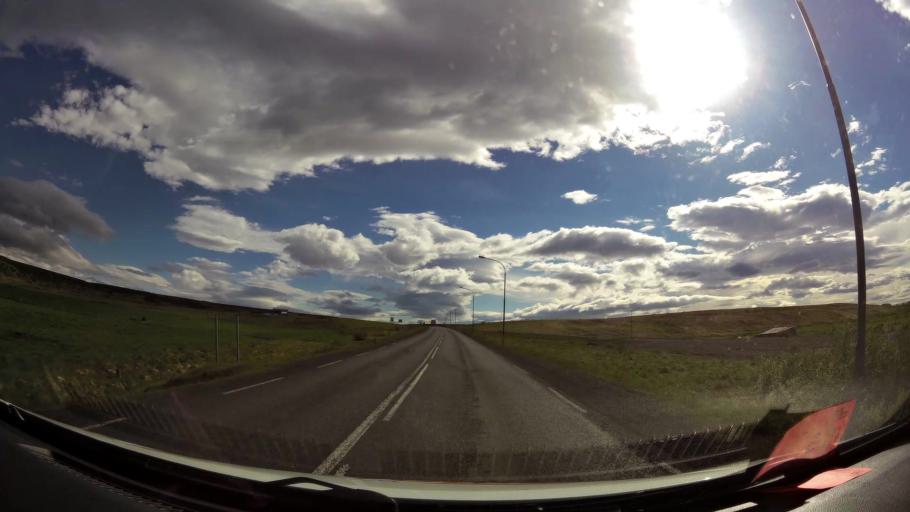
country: IS
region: Northwest
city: Saudarkrokur
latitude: 65.6557
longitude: -20.2850
